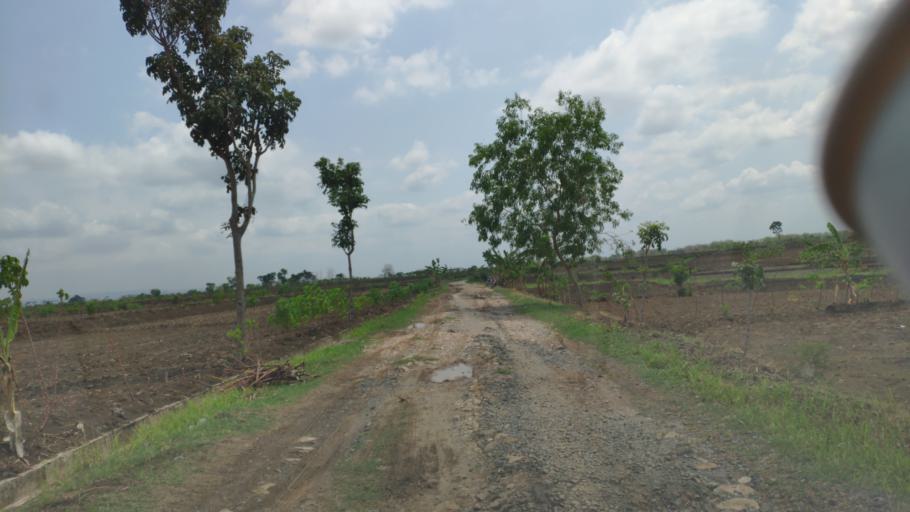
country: ID
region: Central Java
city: Gumiring
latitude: -7.0290
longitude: 111.3781
